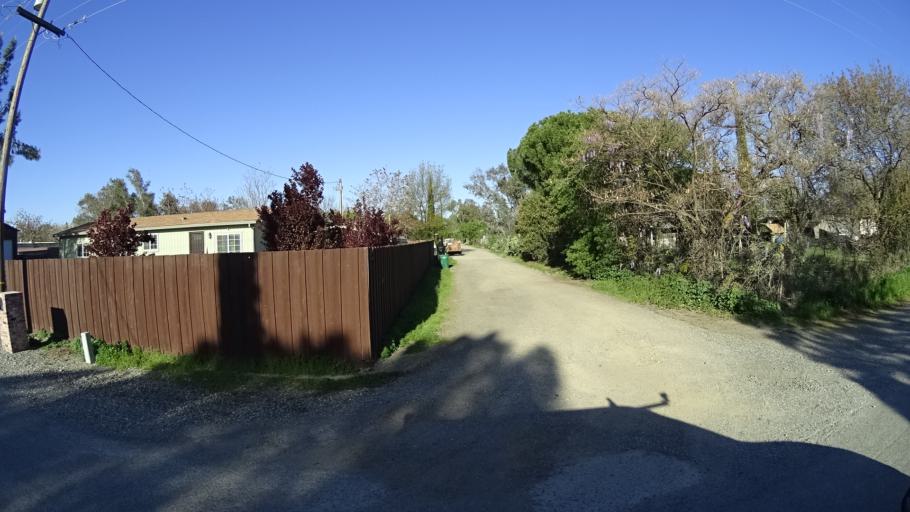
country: US
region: California
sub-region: Glenn County
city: Orland
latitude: 39.7565
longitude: -122.2270
